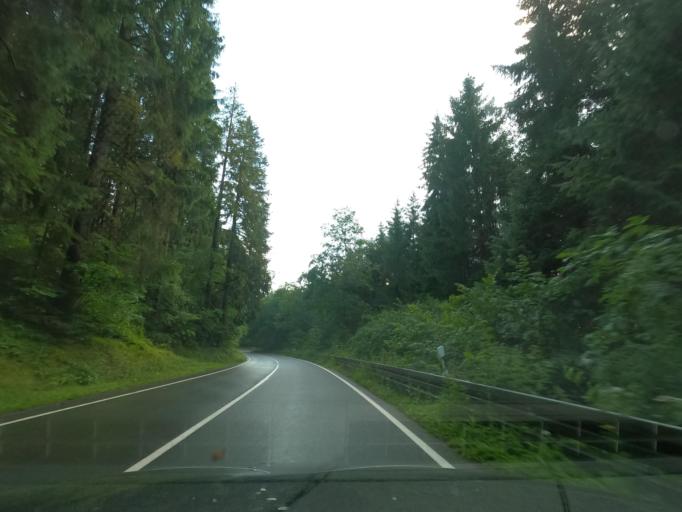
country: DE
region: North Rhine-Westphalia
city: Plettenberg
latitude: 51.2340
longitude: 7.9065
